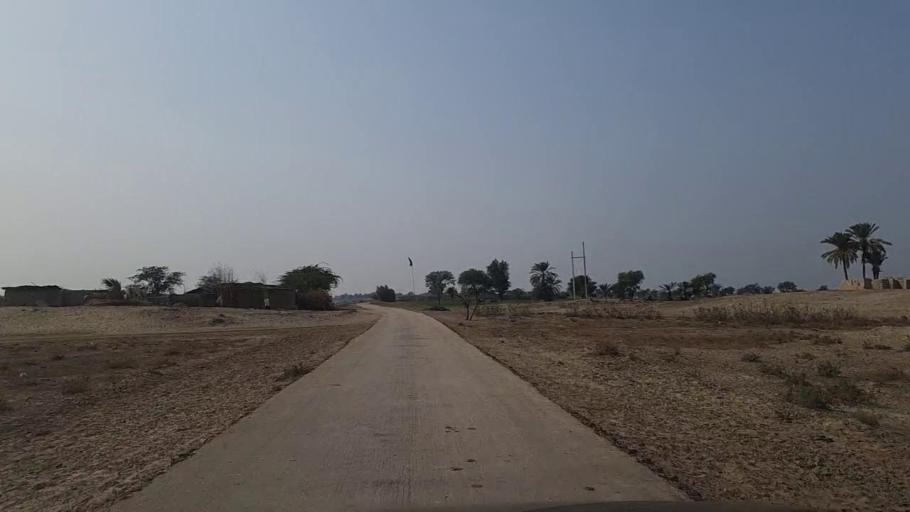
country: PK
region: Sindh
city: Daur
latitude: 26.3858
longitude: 68.4101
